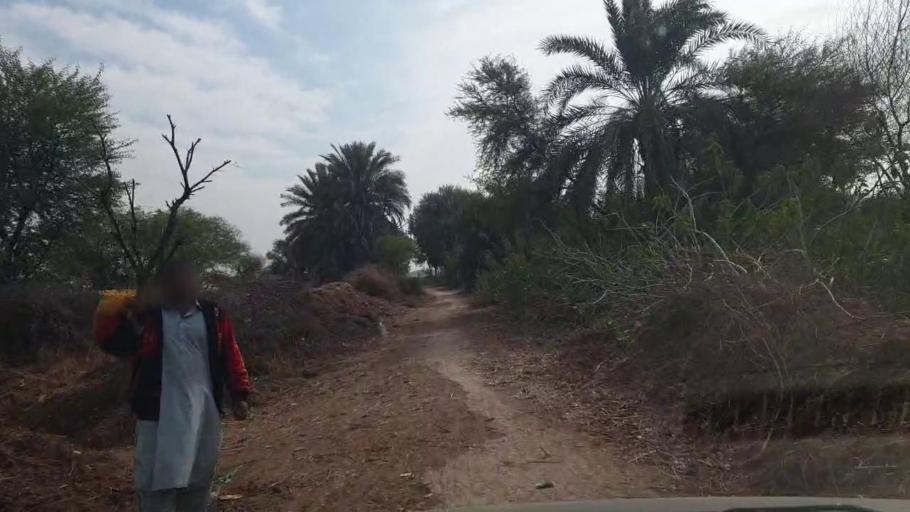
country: PK
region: Sindh
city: Shahdadpur
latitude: 25.9433
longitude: 68.6835
